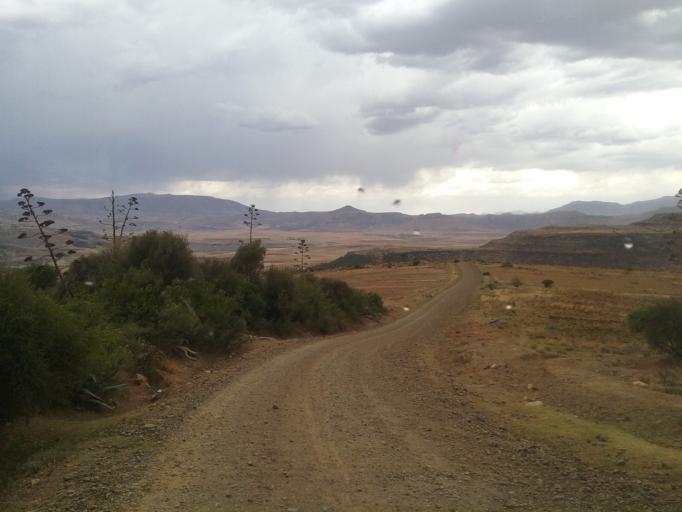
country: LS
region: Quthing
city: Quthing
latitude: -30.3064
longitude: 27.8099
